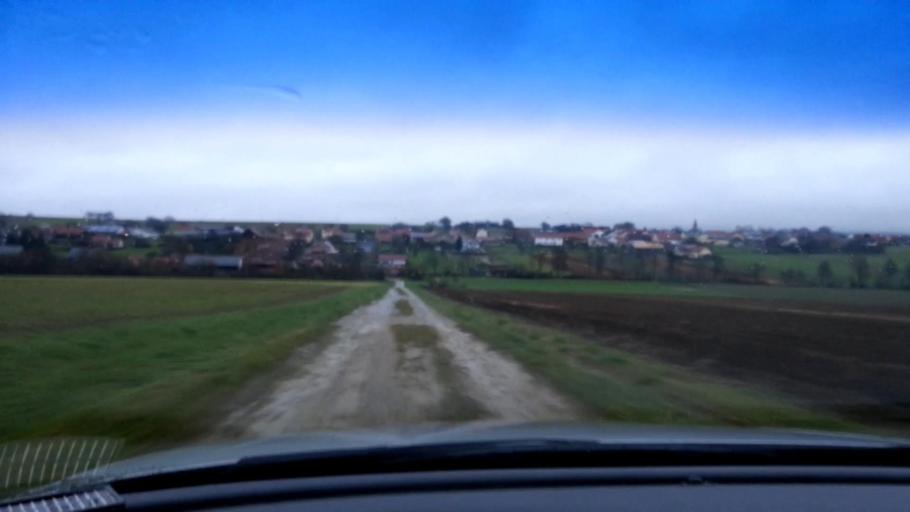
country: DE
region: Bavaria
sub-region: Upper Franconia
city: Schesslitz
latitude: 49.9923
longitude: 10.9926
